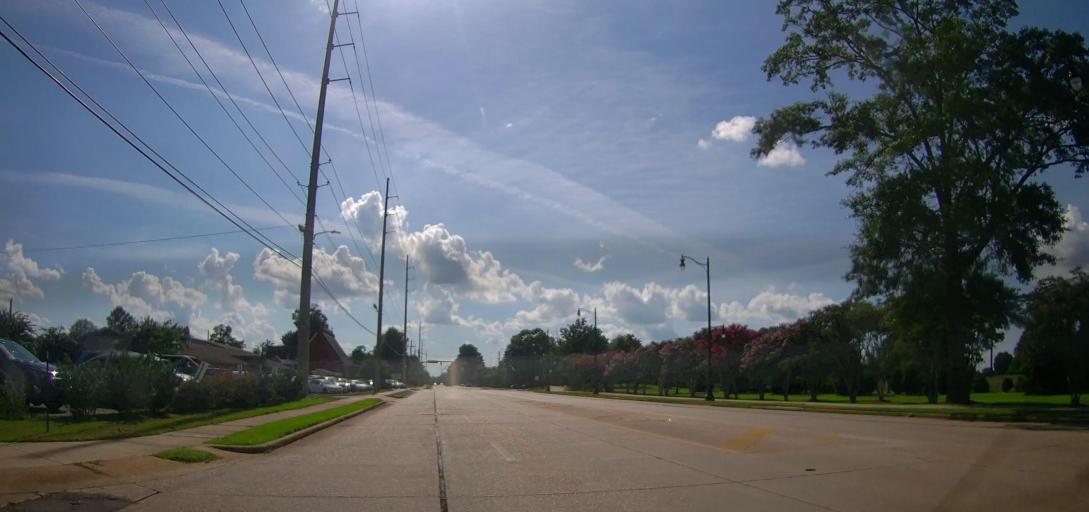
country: US
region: Alabama
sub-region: Tuscaloosa County
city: Holt
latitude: 33.2060
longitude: -87.5163
